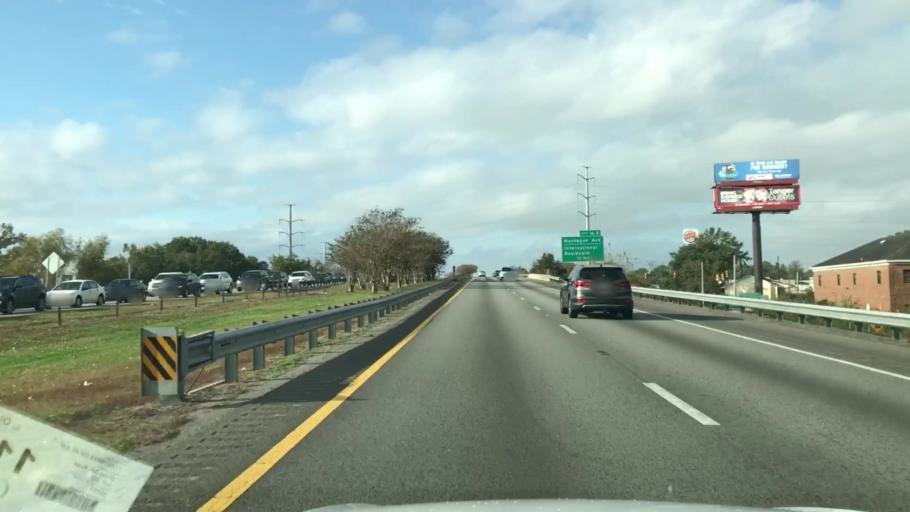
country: US
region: South Carolina
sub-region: Charleston County
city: North Charleston
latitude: 32.8516
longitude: -80.0196
